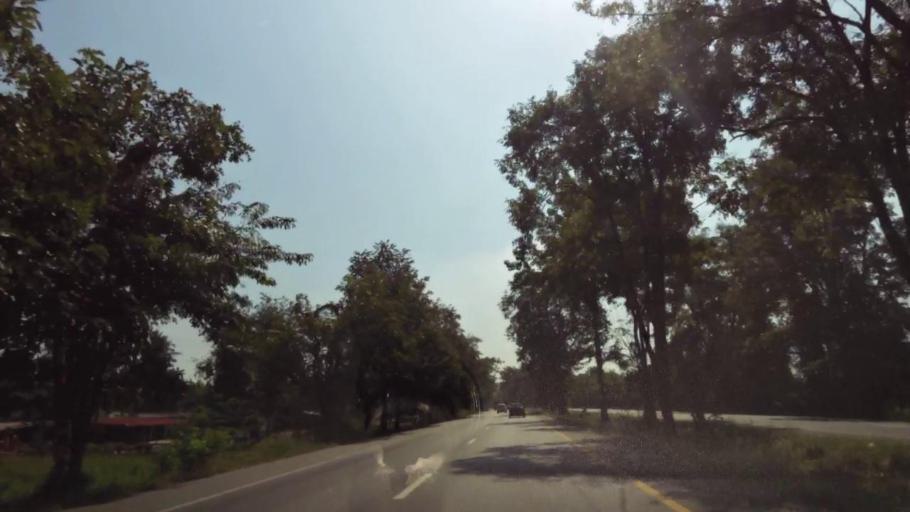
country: TH
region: Phichit
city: Bueng Na Rang
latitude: 16.0253
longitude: 100.1148
